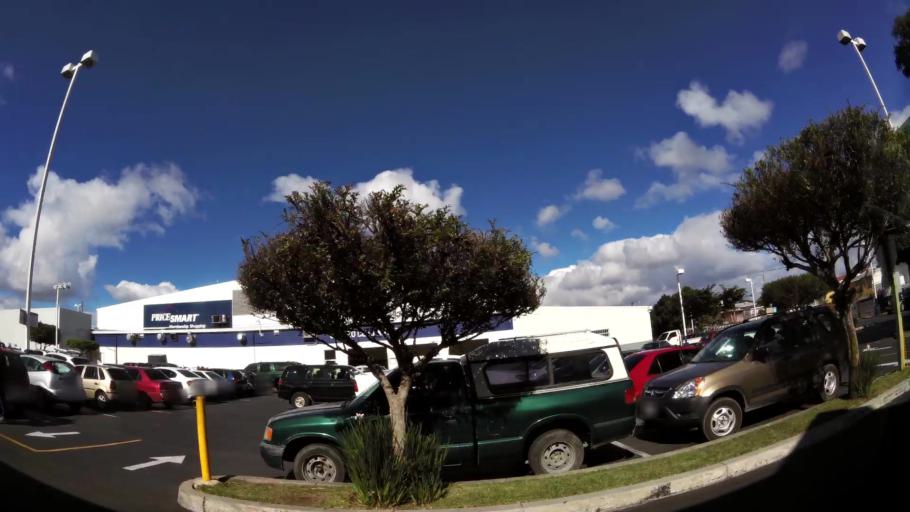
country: GT
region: Guatemala
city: Guatemala City
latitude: 14.6184
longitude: -90.5549
